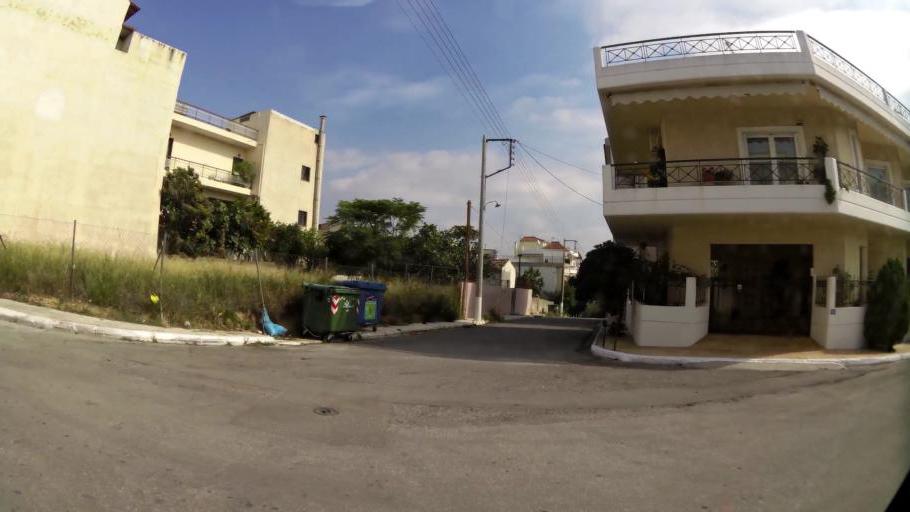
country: GR
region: Attica
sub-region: Nomarchia Dytikis Attikis
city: Zefyri
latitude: 38.0677
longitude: 23.7173
